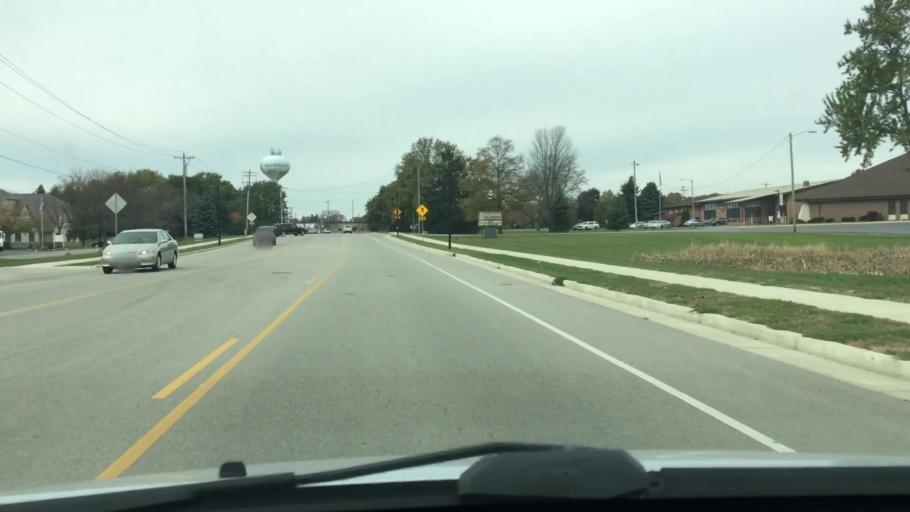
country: US
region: Wisconsin
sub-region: Waukesha County
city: Mukwonago
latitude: 42.8728
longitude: -88.3201
